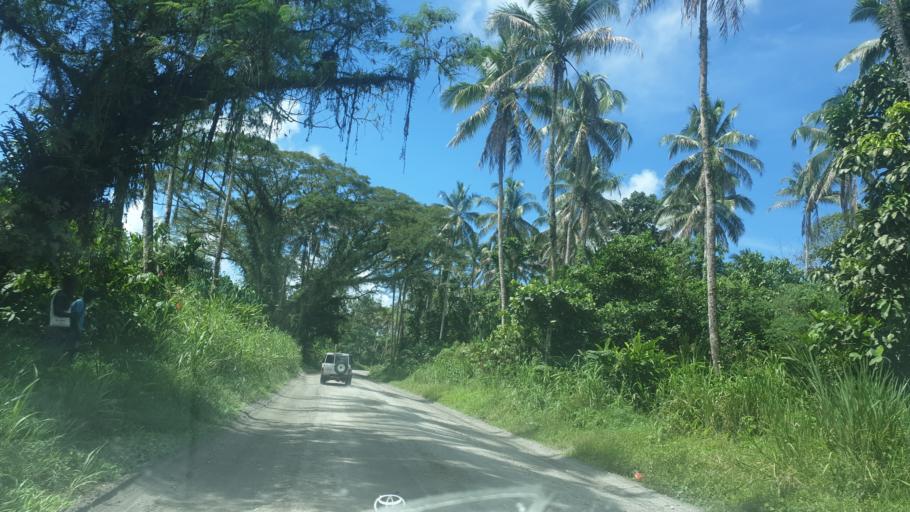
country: PG
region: Bougainville
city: Panguna
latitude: -6.7387
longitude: 155.6717
